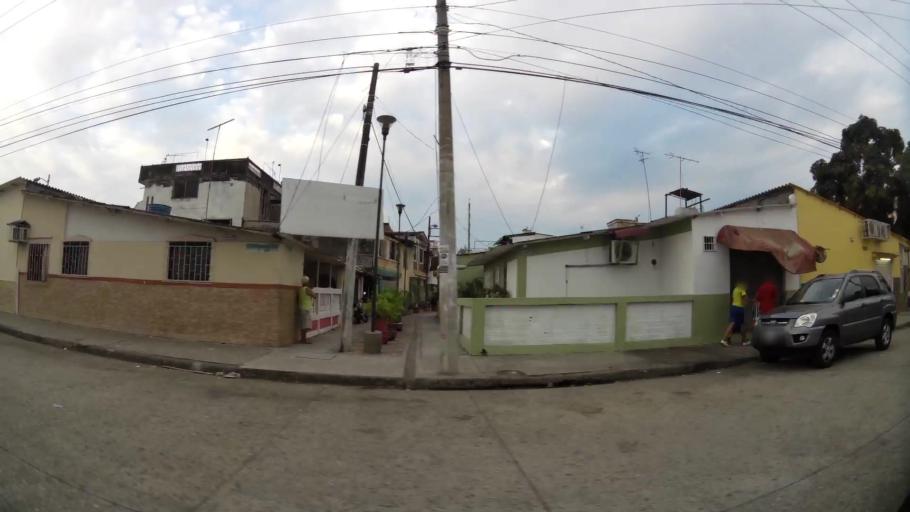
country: EC
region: Guayas
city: Guayaquil
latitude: -2.2394
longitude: -79.8886
